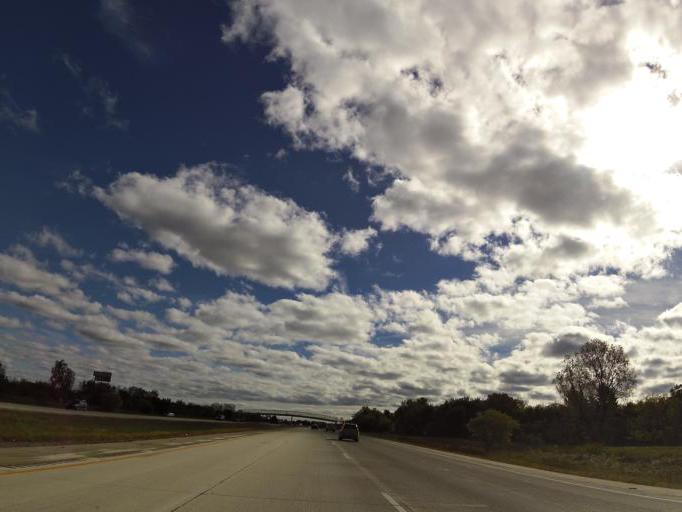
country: US
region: Michigan
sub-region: Genesee County
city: Burton
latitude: 43.0194
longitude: -83.5938
